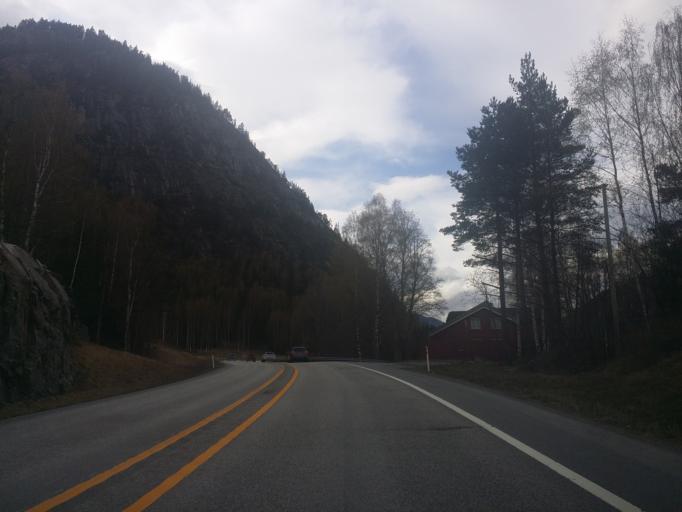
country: NO
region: Buskerud
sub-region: Nes
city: Nesbyen
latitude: 60.4604
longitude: 9.2584
